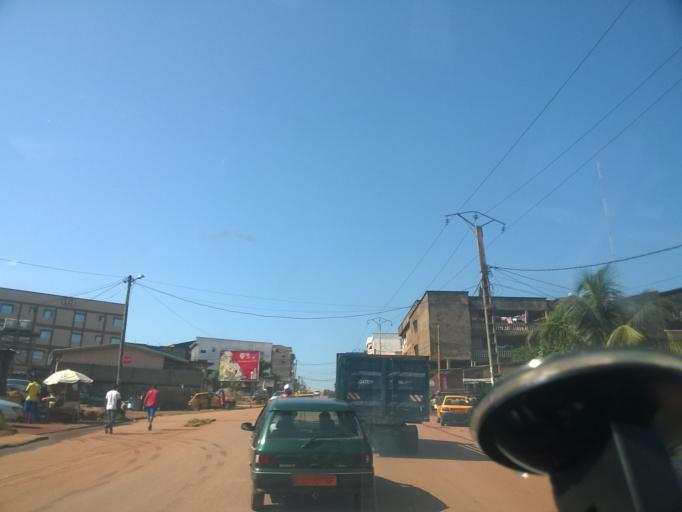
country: CM
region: Centre
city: Yaounde
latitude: 3.8310
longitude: 11.4820
